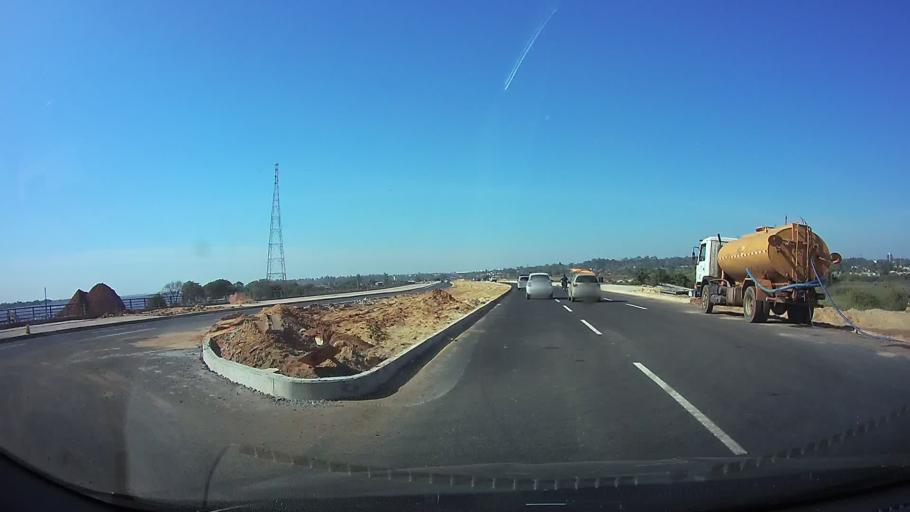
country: PY
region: Asuncion
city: Asuncion
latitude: -25.2463
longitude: -57.5951
